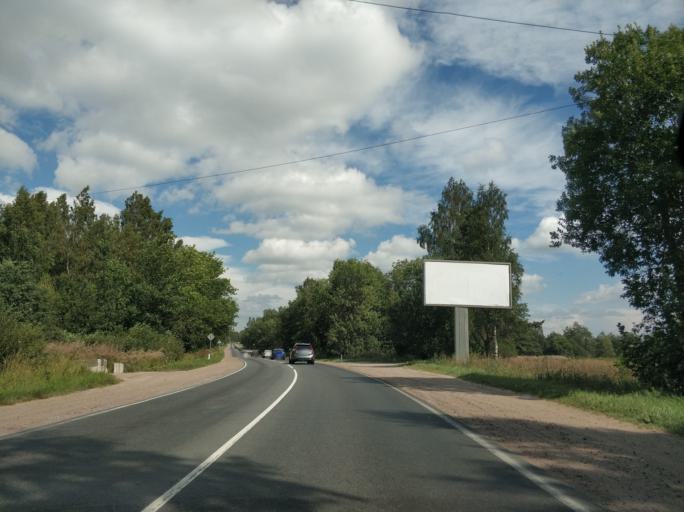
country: RU
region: Leningrad
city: Vsevolozhsk
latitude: 60.0389
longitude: 30.6679
